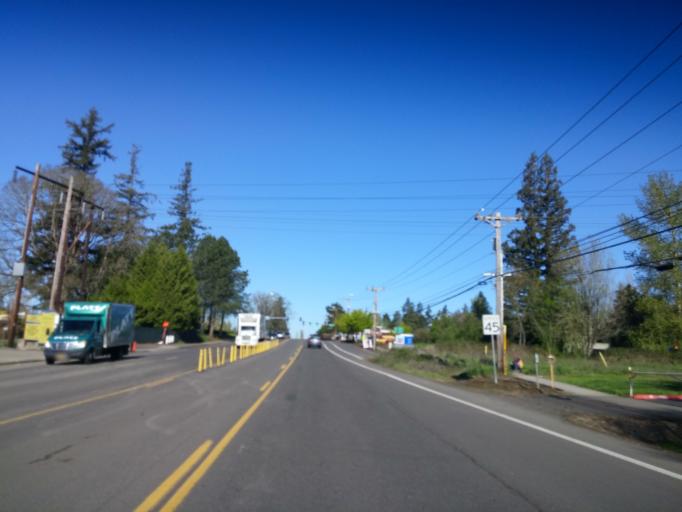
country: US
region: Oregon
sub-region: Washington County
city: Cedar Mill
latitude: 45.5141
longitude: -122.8299
